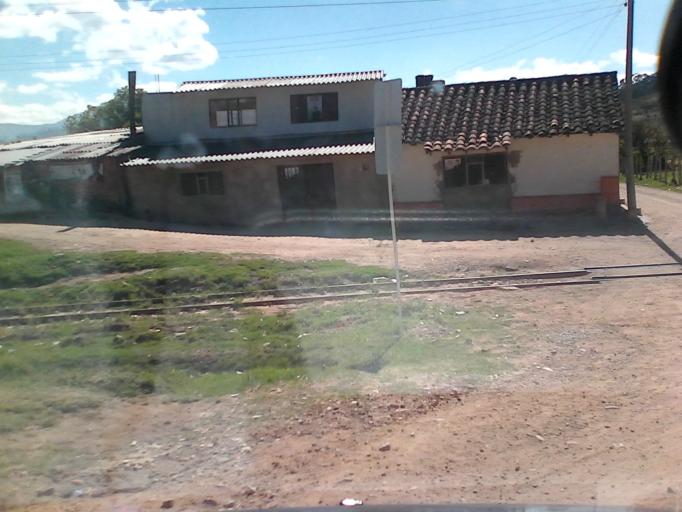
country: CO
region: Boyaca
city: Duitama
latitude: 5.7955
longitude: -73.0419
